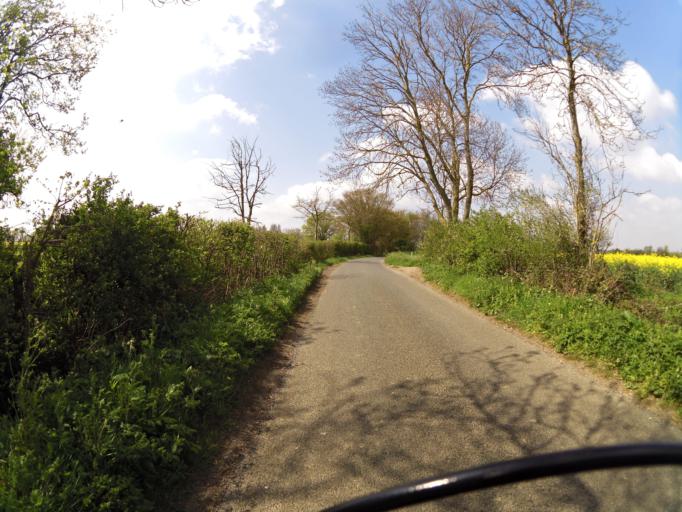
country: GB
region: England
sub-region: Suffolk
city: Hadleigh
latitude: 52.0809
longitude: 0.9837
